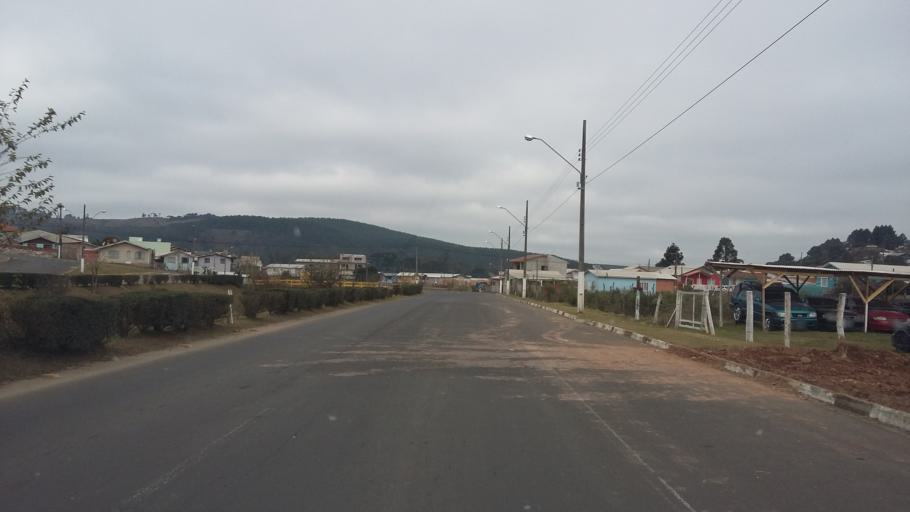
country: BR
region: Santa Catarina
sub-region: Lages
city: Lages
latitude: -27.8324
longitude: -50.3208
